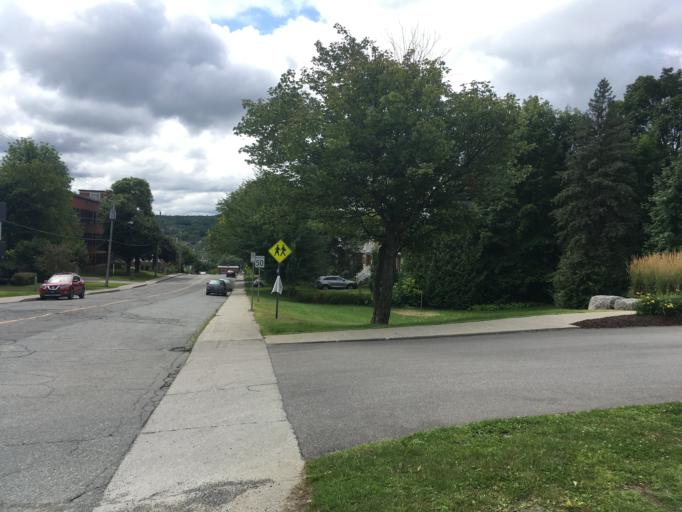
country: CA
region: Quebec
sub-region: Estrie
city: Sherbrooke
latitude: 45.4012
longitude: -71.9080
